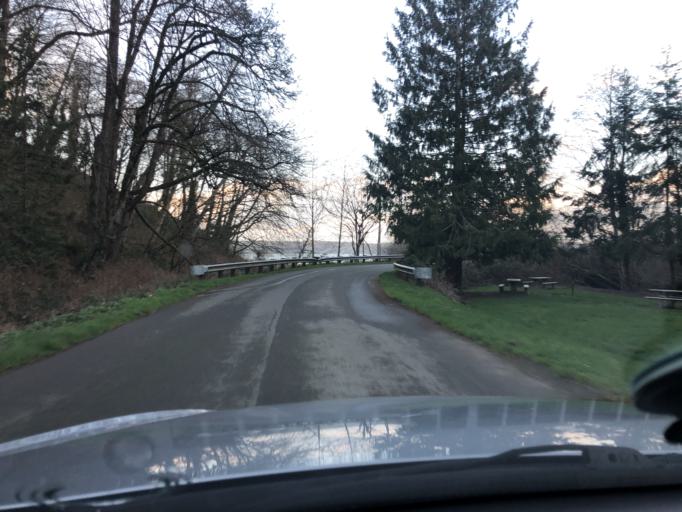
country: US
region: Washington
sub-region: Pierce County
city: Tacoma
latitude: 47.3191
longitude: -122.4138
